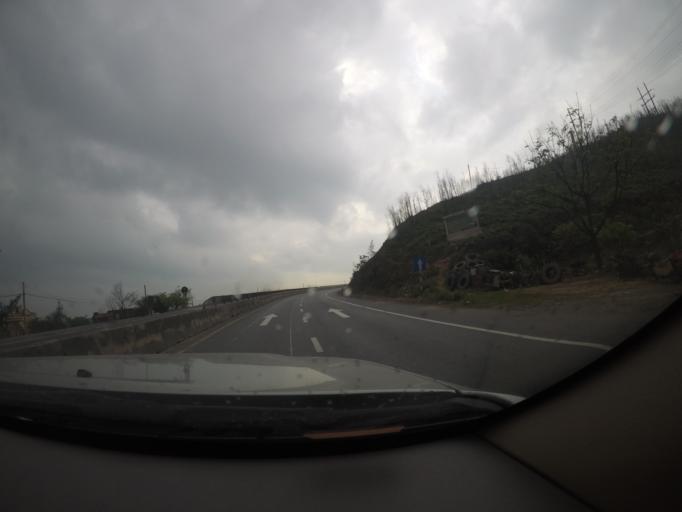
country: VN
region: Ha Tinh
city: Ky Anh
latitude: 17.9864
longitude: 106.4796
